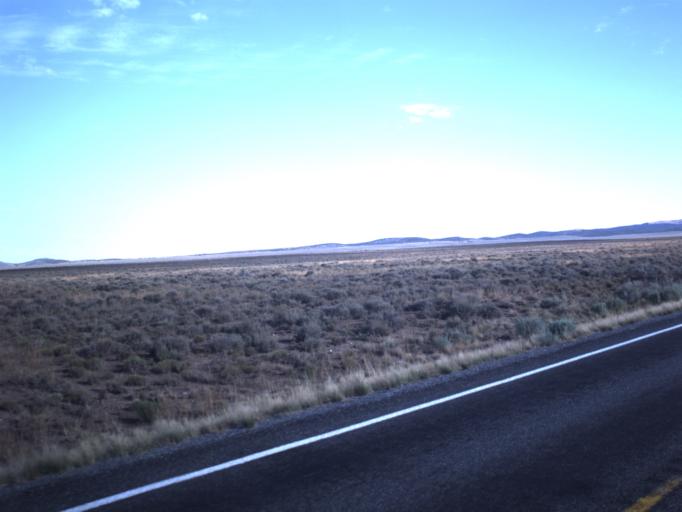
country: US
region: Utah
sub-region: Iron County
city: Enoch
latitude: 37.9217
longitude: -113.0315
